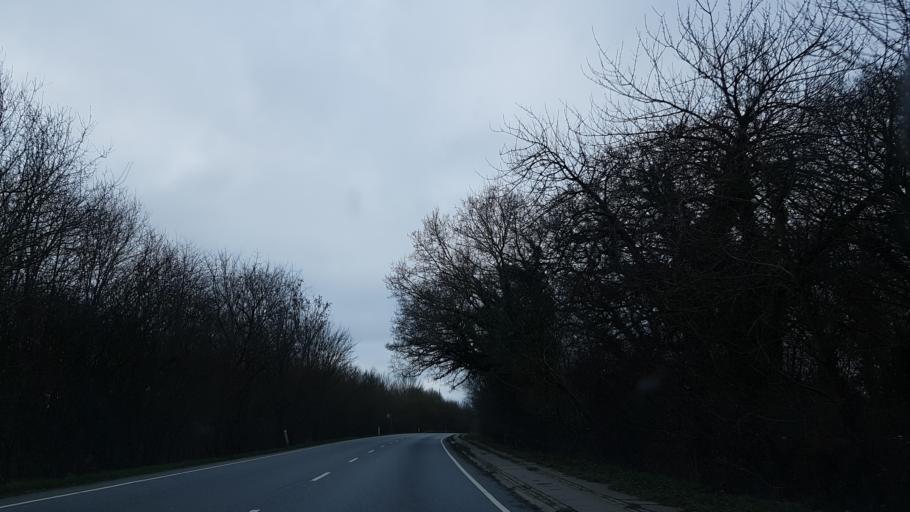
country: DK
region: Zealand
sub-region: Kalundborg Kommune
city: Svebolle
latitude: 55.6535
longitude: 11.2977
